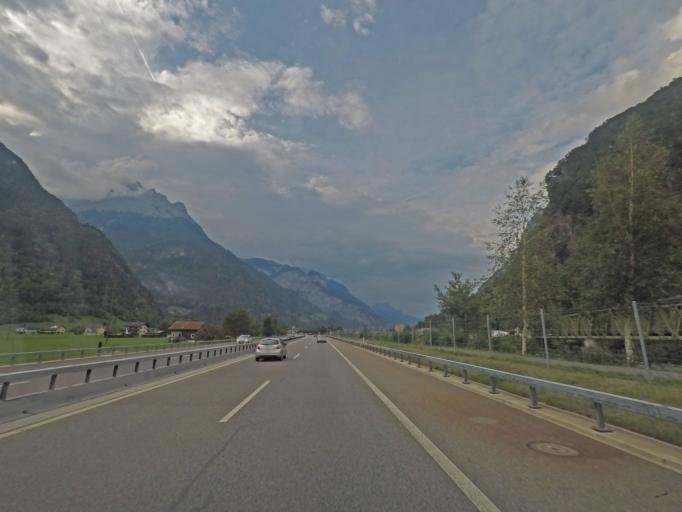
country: CH
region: Uri
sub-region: Uri
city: Erstfeld
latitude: 46.8109
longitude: 8.6586
